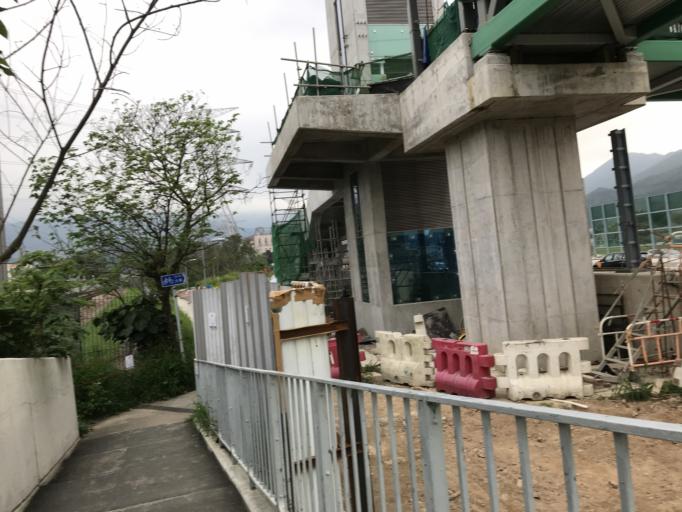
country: HK
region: Tai Po
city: Tai Po
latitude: 22.4682
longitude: 114.1527
